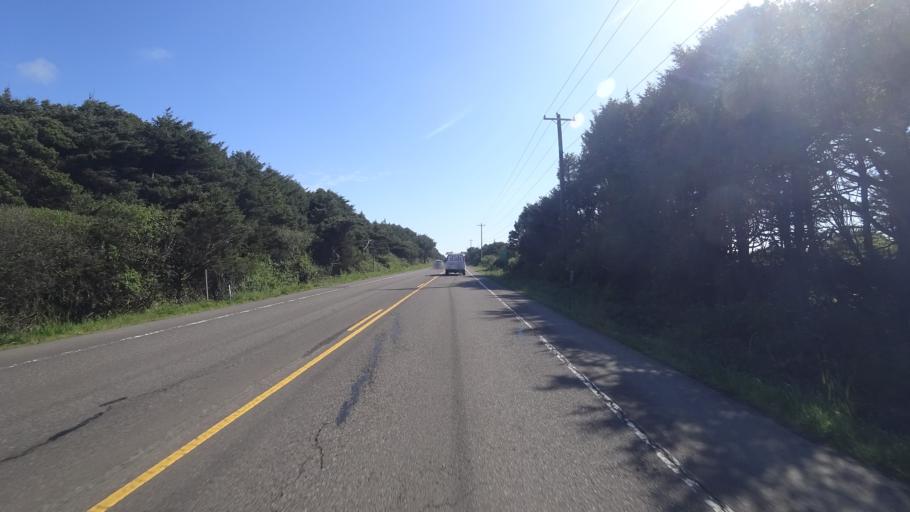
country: US
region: Oregon
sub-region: Lincoln County
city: Newport
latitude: 44.5627
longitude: -124.0698
